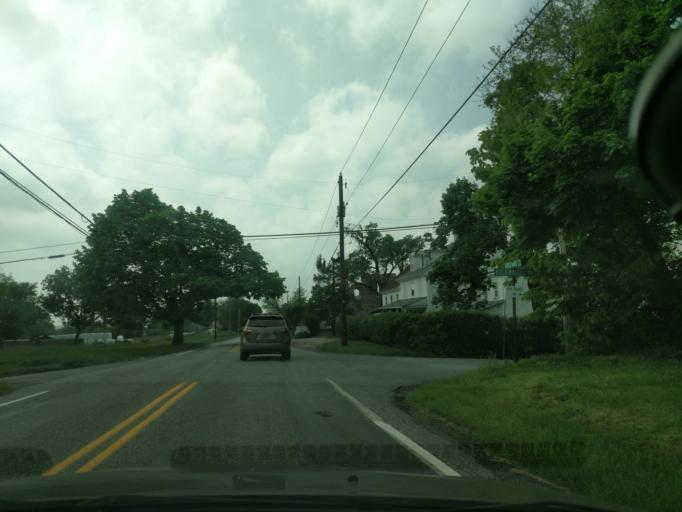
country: US
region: Pennsylvania
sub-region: Chester County
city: Spring City
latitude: 40.1570
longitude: -75.5756
